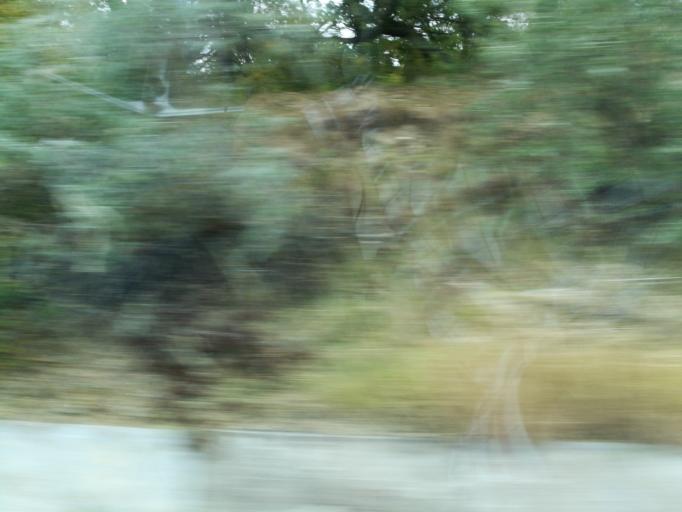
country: RO
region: Tulcea
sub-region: Comuna Horia
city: Horia
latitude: 44.9880
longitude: 28.4541
